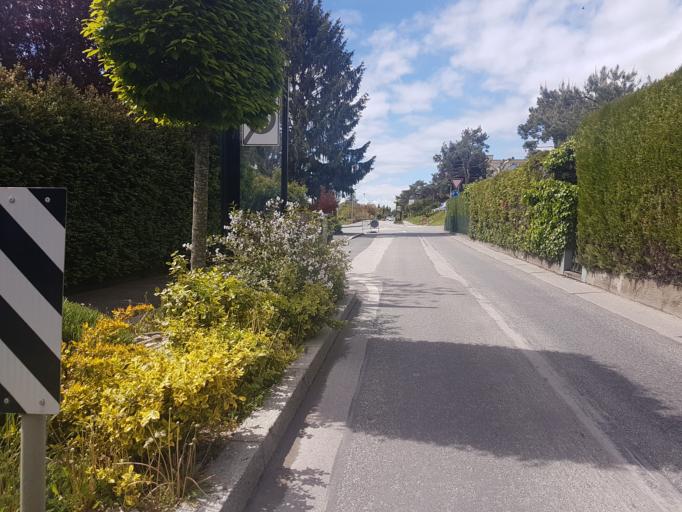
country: CH
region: Vaud
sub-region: Nyon District
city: Rolle
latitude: 46.4599
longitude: 6.3337
